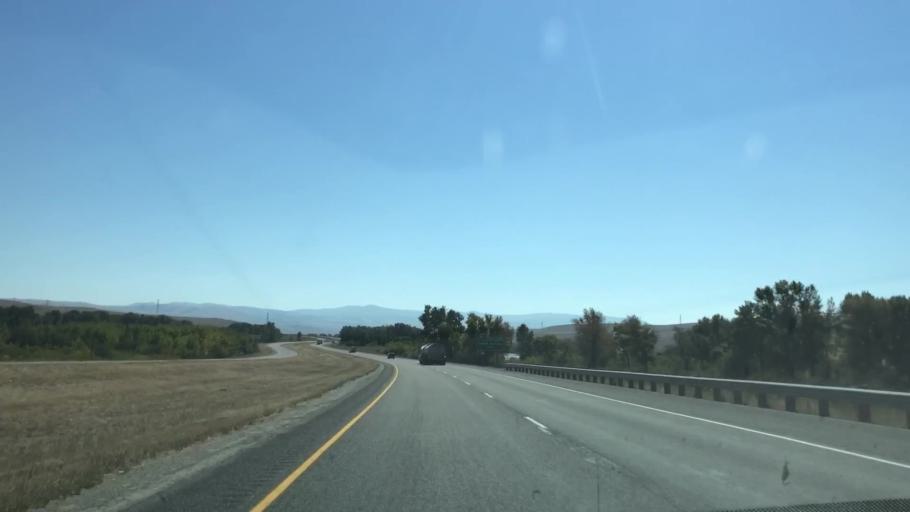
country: US
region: Montana
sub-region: Powell County
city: Deer Lodge
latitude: 46.5210
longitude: -112.8067
